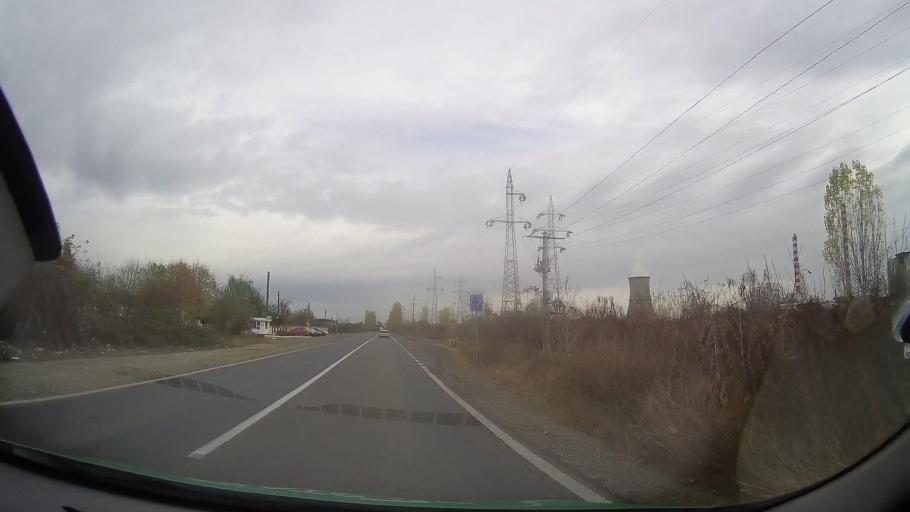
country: RO
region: Prahova
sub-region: Comuna Bucov
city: Bucov
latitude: 44.9545
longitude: 26.0741
